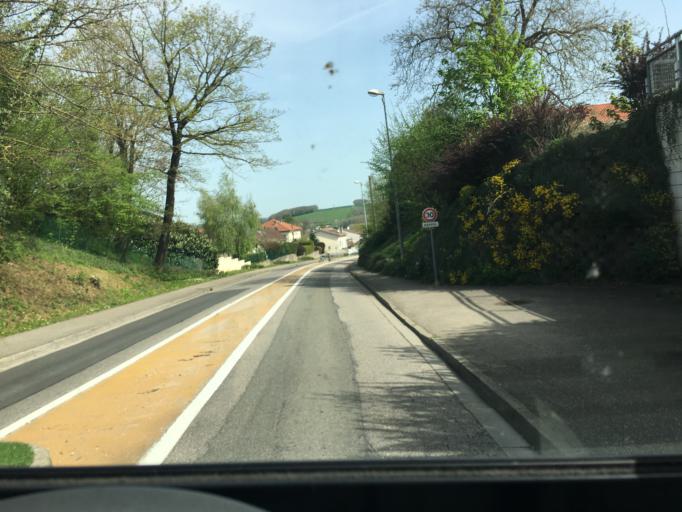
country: FR
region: Lorraine
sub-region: Departement de Meurthe-et-Moselle
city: Saint-Nicolas-de-Port
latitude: 48.6265
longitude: 6.2945
